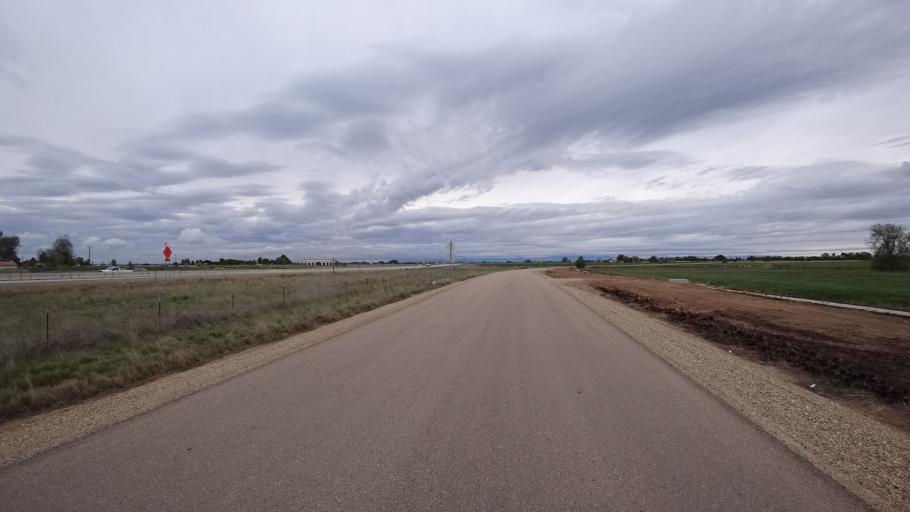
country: US
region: Idaho
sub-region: Ada County
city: Star
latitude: 43.6683
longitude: -116.4701
